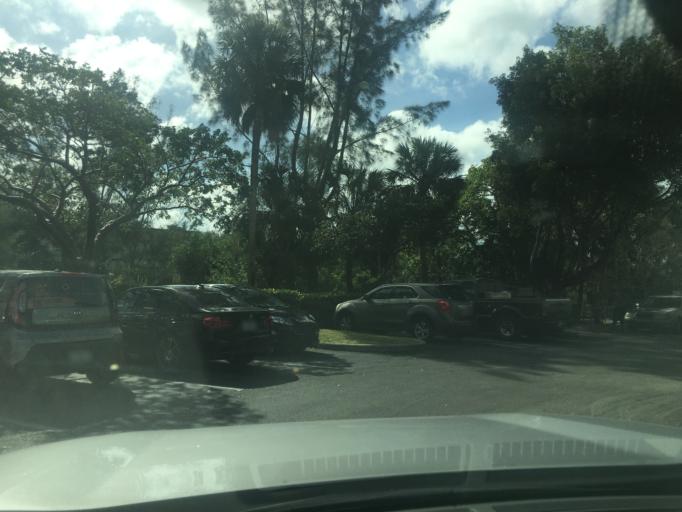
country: US
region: Florida
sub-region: Broward County
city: Broadview Park
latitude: 26.0722
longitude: -80.1801
